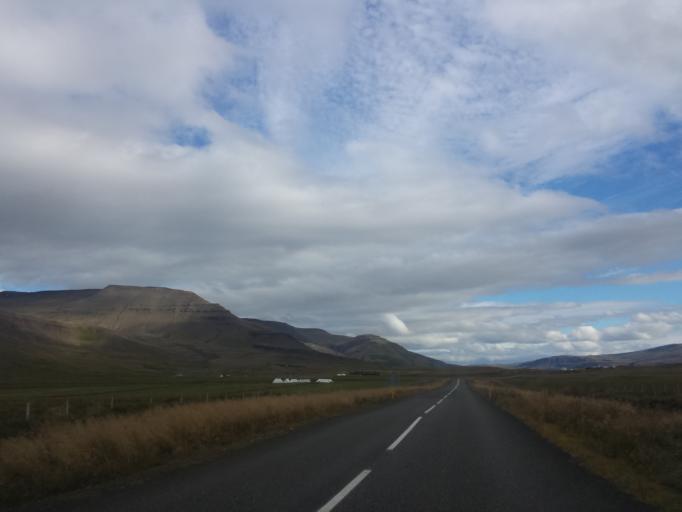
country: IS
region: West
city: Borgarnes
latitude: 64.4219
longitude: -21.7861
